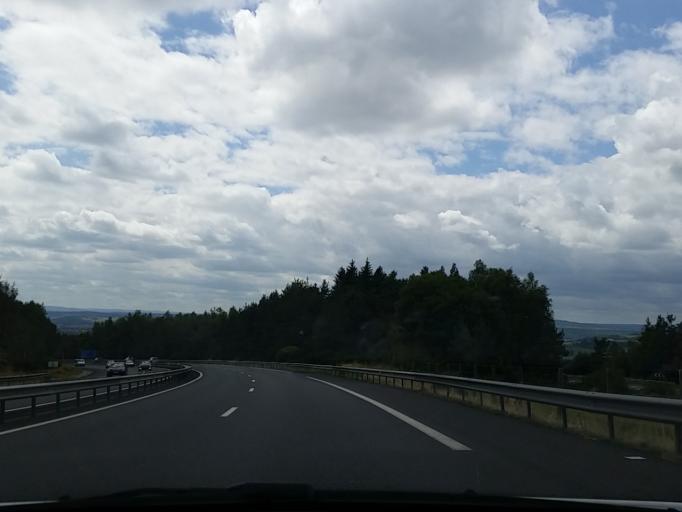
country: FR
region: Auvergne
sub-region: Departement du Cantal
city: Saint-Flour
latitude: 45.0881
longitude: 3.1178
